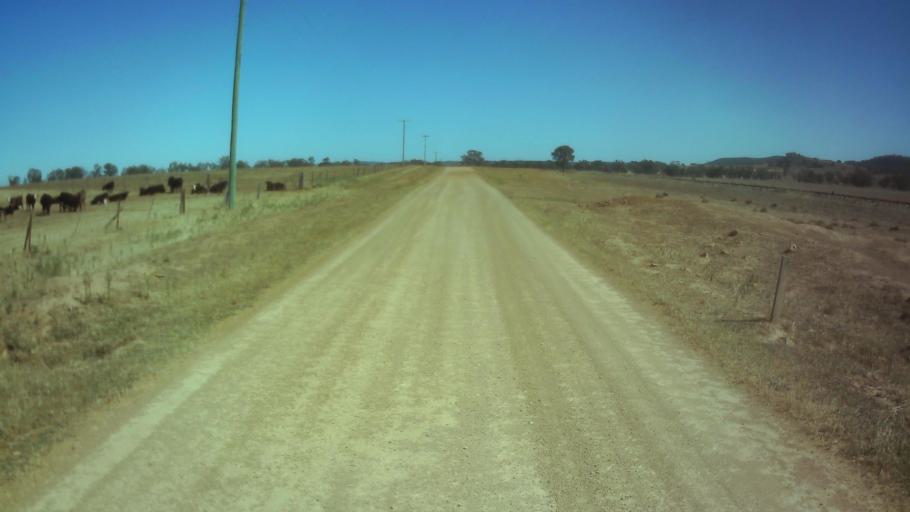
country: AU
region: New South Wales
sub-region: Weddin
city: Grenfell
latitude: -33.9516
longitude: 148.2999
